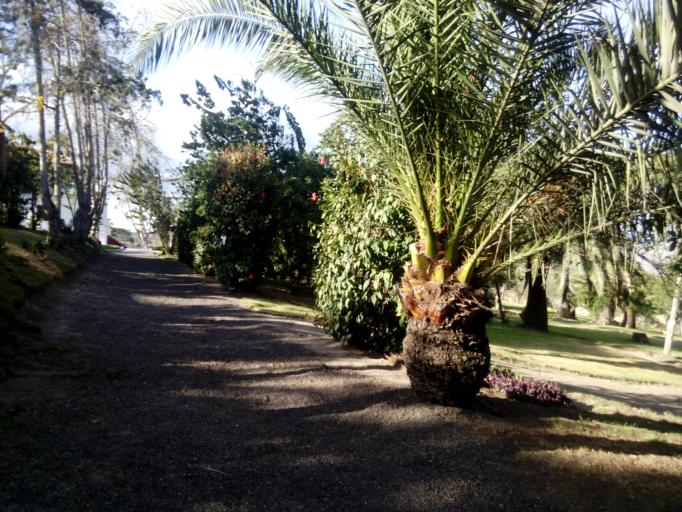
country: EC
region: Imbabura
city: Ibarra
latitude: 0.4061
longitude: -78.1758
